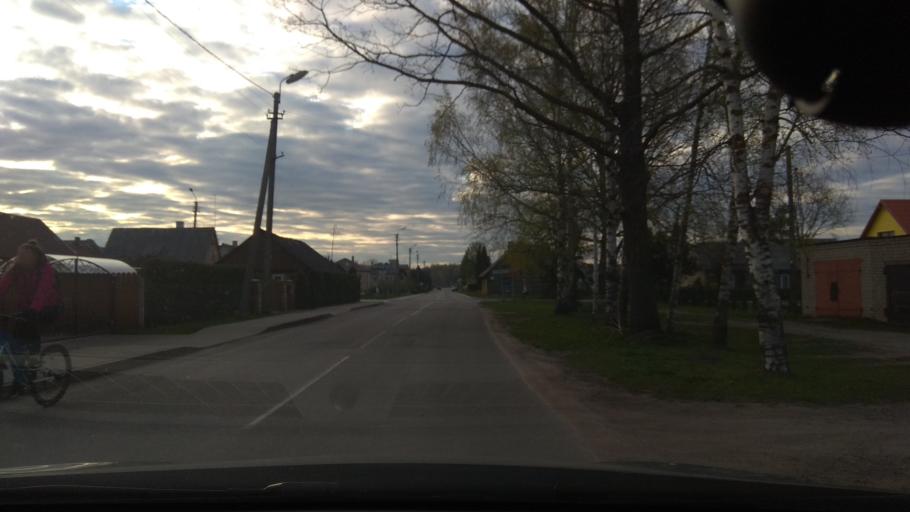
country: LT
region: Siauliu apskritis
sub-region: Joniskis
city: Joniskis
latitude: 56.2455
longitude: 23.6134
